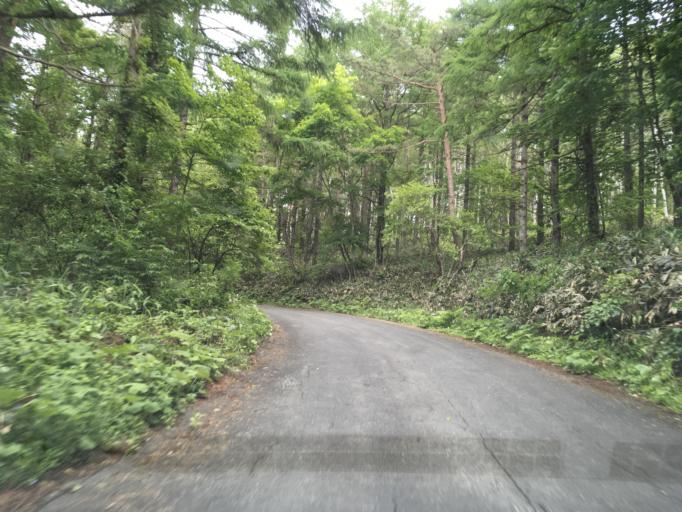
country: JP
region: Iwate
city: Mizusawa
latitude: 39.1213
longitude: 141.3023
